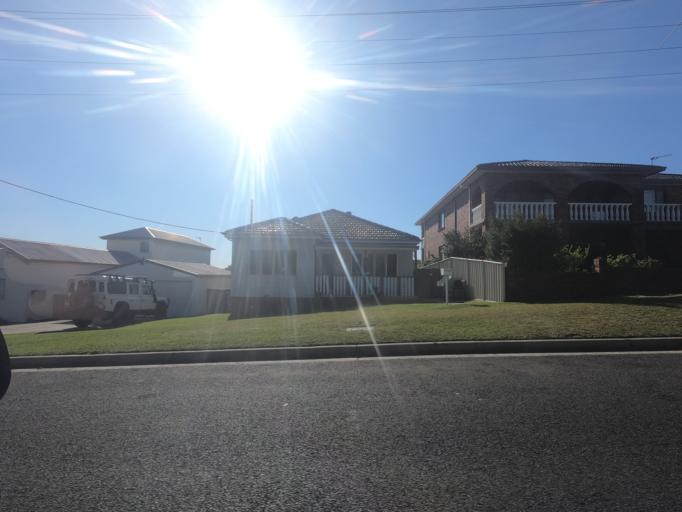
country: AU
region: New South Wales
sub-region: Wollongong
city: Corrimal
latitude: -34.3760
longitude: 150.8879
